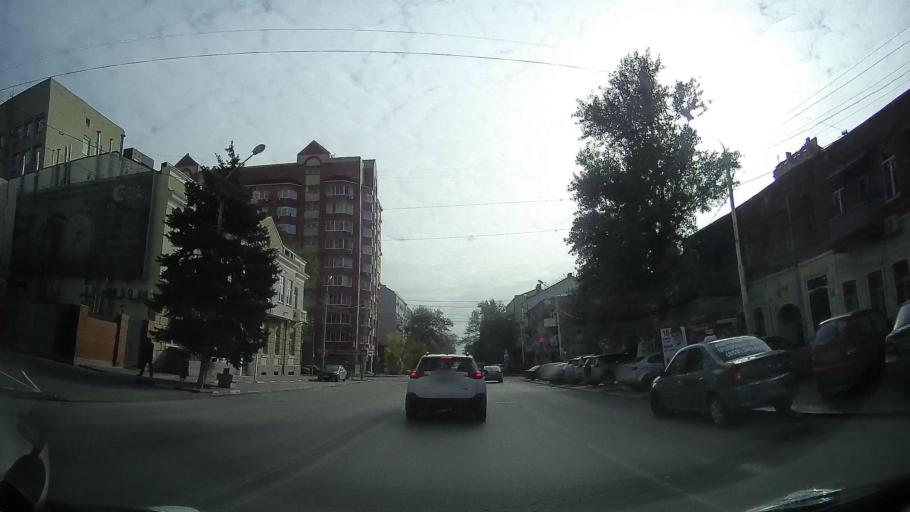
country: RU
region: Rostov
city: Rostov-na-Donu
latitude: 47.2284
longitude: 39.7191
